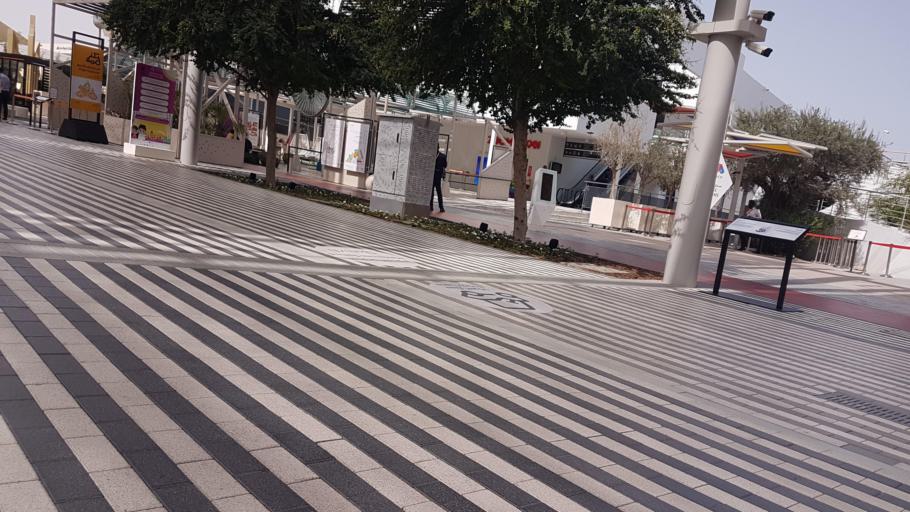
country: AE
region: Dubai
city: Dubai
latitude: 24.9646
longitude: 55.1509
